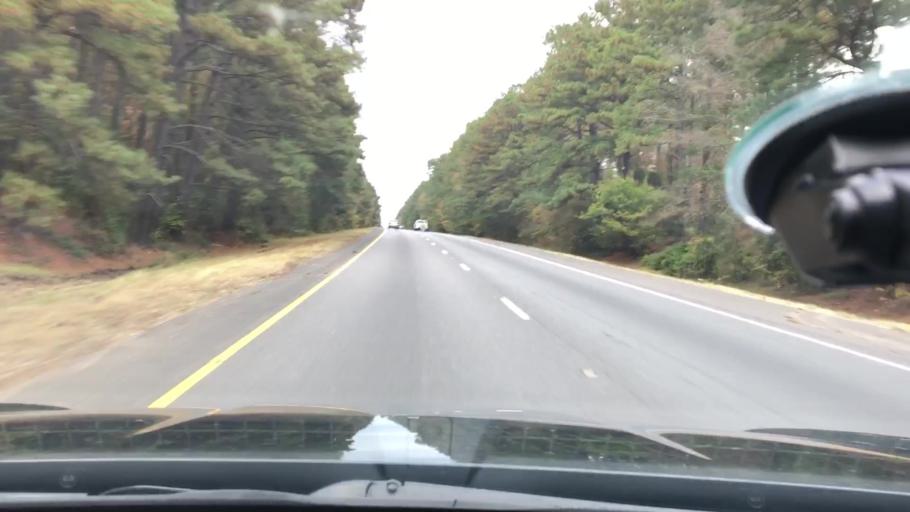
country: US
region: Arkansas
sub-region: Hot Spring County
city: Malvern
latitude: 34.2876
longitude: -92.9544
